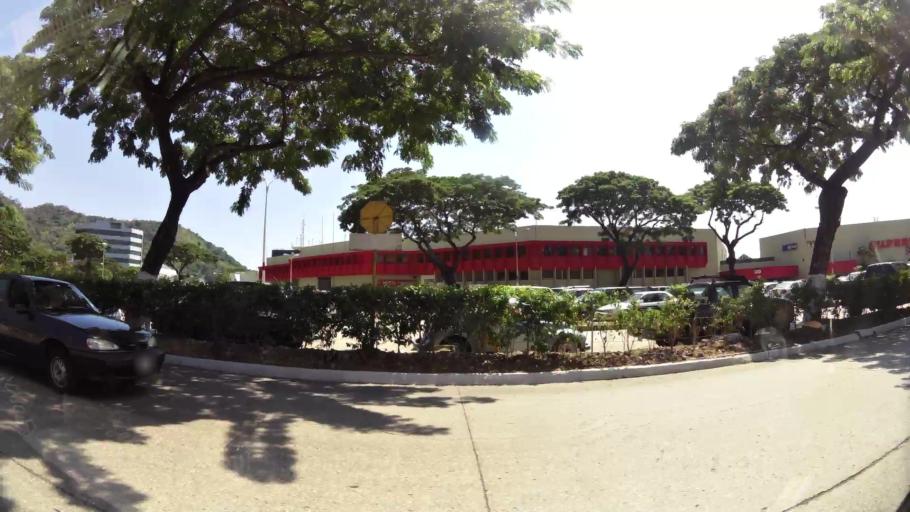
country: EC
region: Guayas
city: Guayaquil
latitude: -2.1698
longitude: -79.9159
